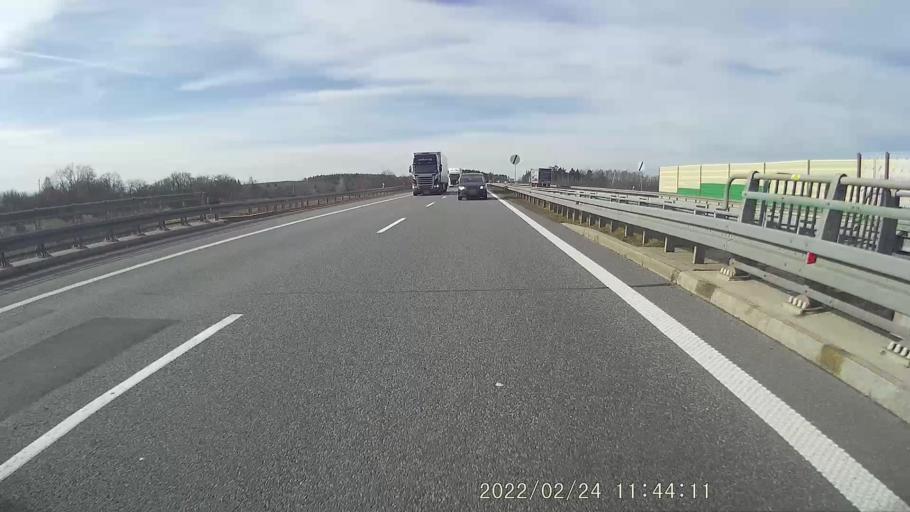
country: PL
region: Lower Silesian Voivodeship
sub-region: Powiat polkowicki
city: Radwanice
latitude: 51.5471
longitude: 15.9256
